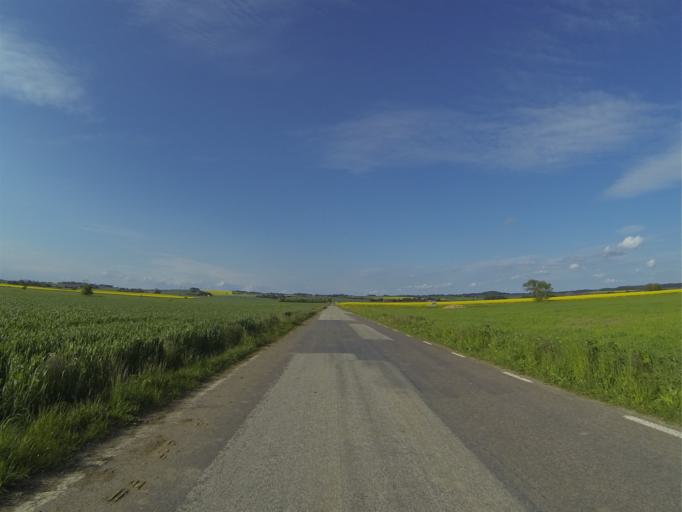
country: SE
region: Skane
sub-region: Staffanstorps Kommun
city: Staffanstorp
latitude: 55.6674
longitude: 13.2726
